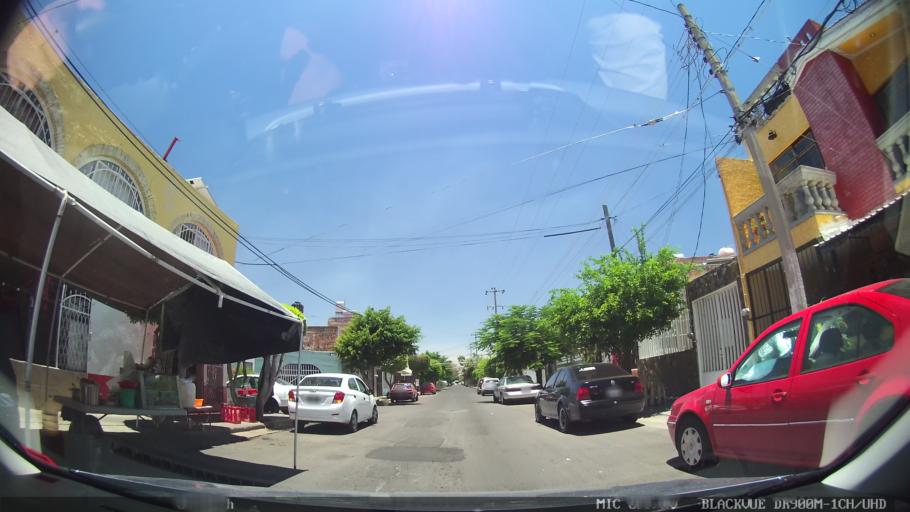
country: MX
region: Jalisco
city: Tlaquepaque
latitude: 20.6784
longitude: -103.2826
